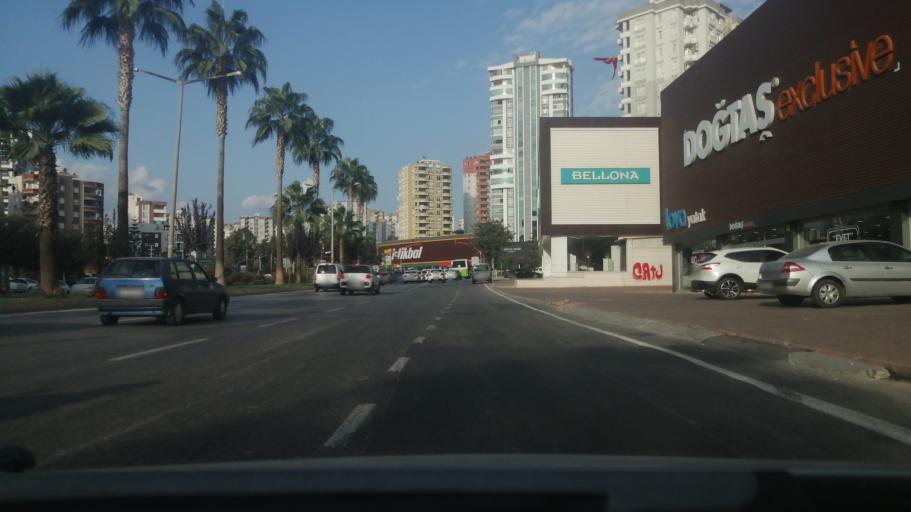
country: TR
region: Adana
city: Seyhan
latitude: 37.0343
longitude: 35.2563
